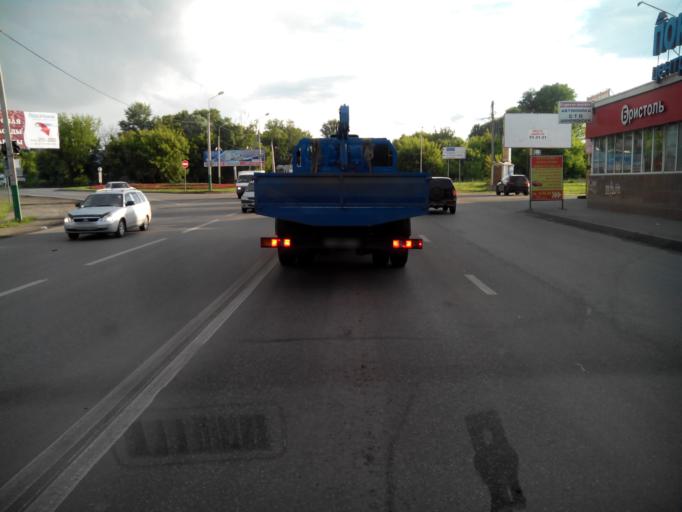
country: RU
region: Penza
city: Penza
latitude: 53.1503
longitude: 44.9667
